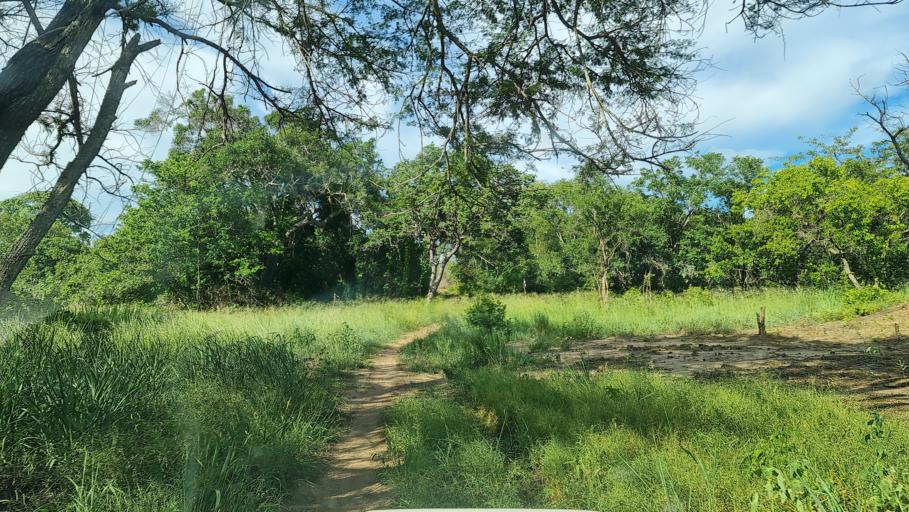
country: MZ
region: Nampula
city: Ilha de Mocambique
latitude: -15.5034
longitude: 40.1571
